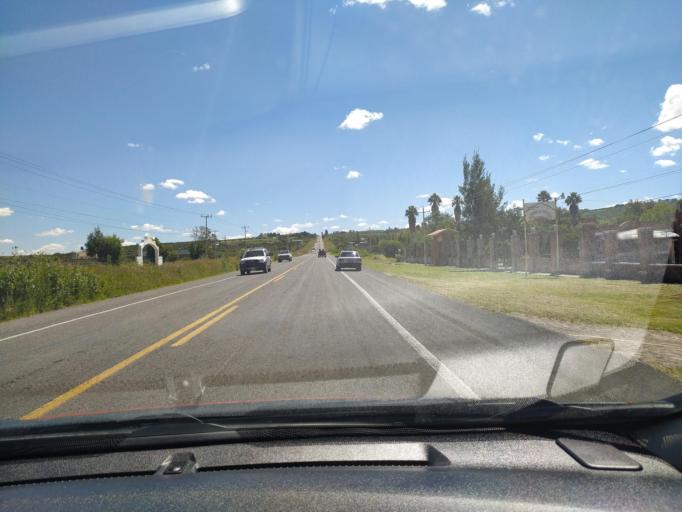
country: MX
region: Jalisco
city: San Miguel el Alto
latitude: 21.0195
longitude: -102.3452
